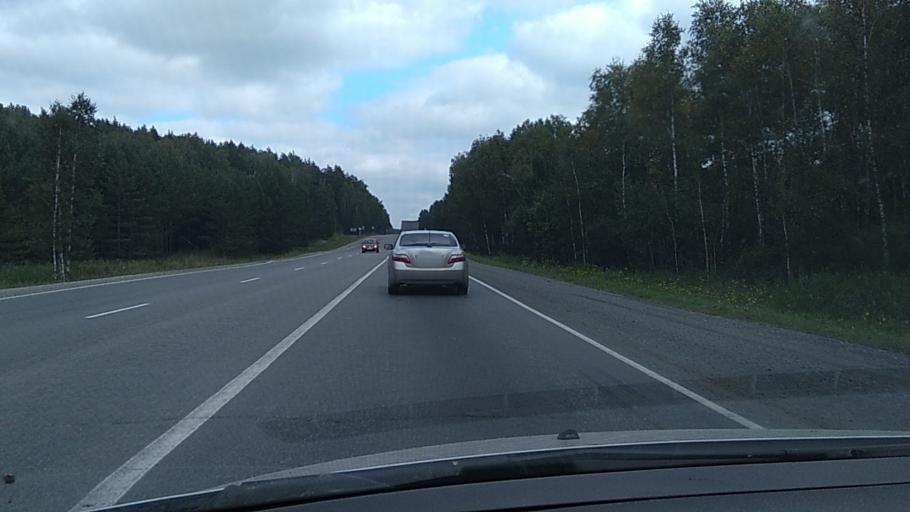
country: RU
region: Chelyabinsk
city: Miass
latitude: 54.9445
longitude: 60.0757
